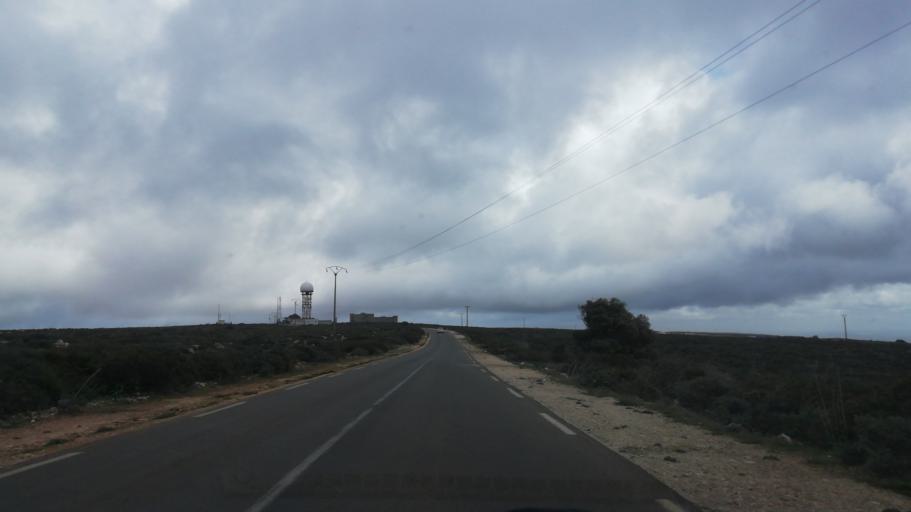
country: DZ
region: Oran
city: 'Ain el Turk
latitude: 35.6926
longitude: -0.7765
